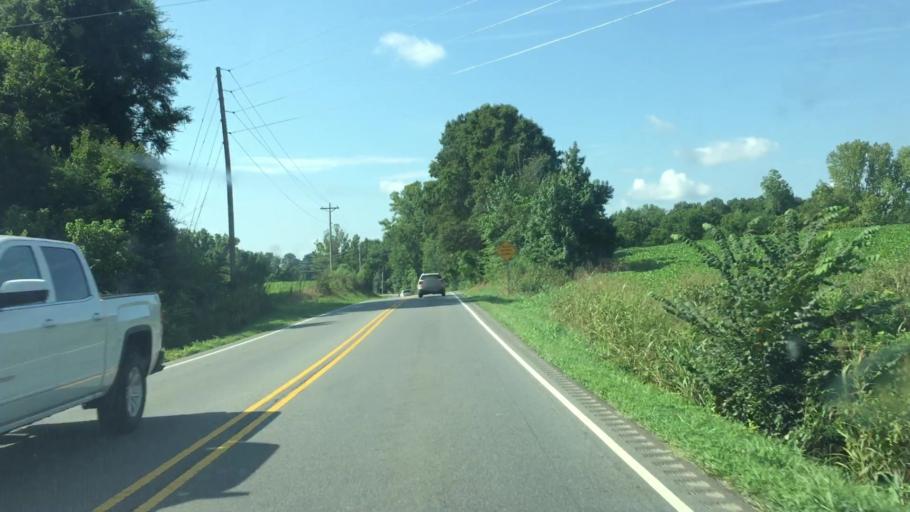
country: US
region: North Carolina
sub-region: Union County
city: Fairview
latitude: 35.1486
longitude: -80.5522
